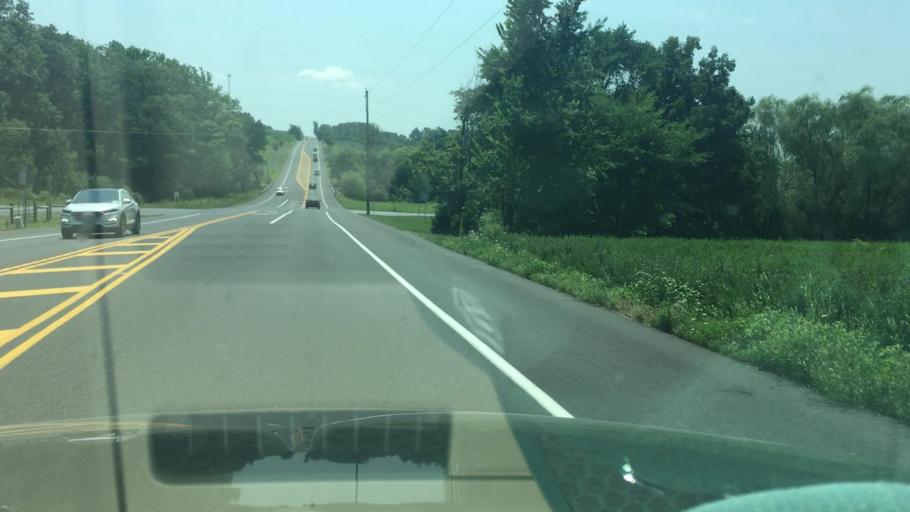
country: US
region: Pennsylvania
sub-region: Carbon County
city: Lehighton
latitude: 40.7086
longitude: -75.7623
